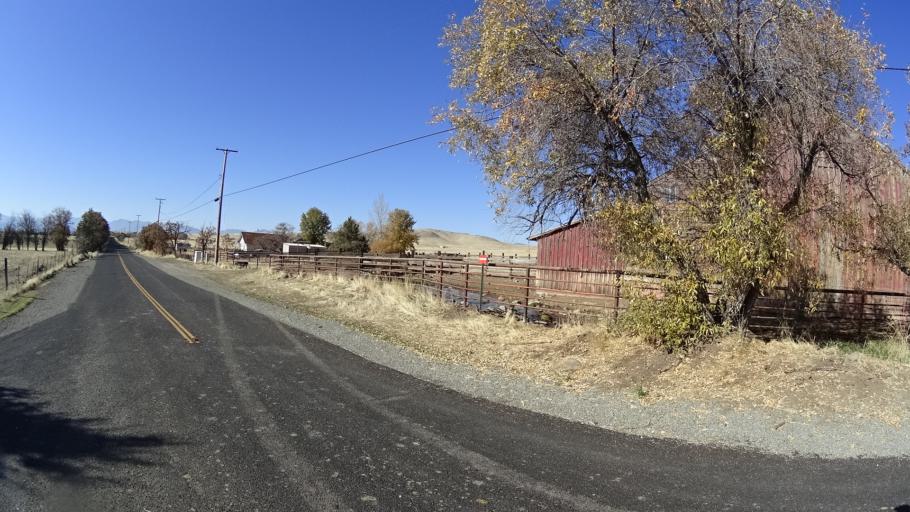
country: US
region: California
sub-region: Siskiyou County
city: Montague
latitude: 41.7263
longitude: -122.3892
